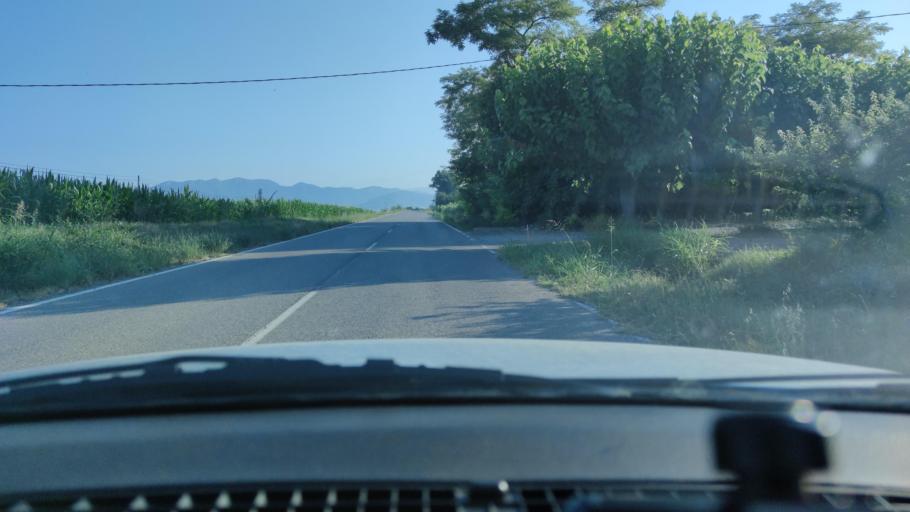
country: ES
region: Catalonia
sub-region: Provincia de Lleida
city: Balaguer
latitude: 41.8034
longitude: 0.8259
